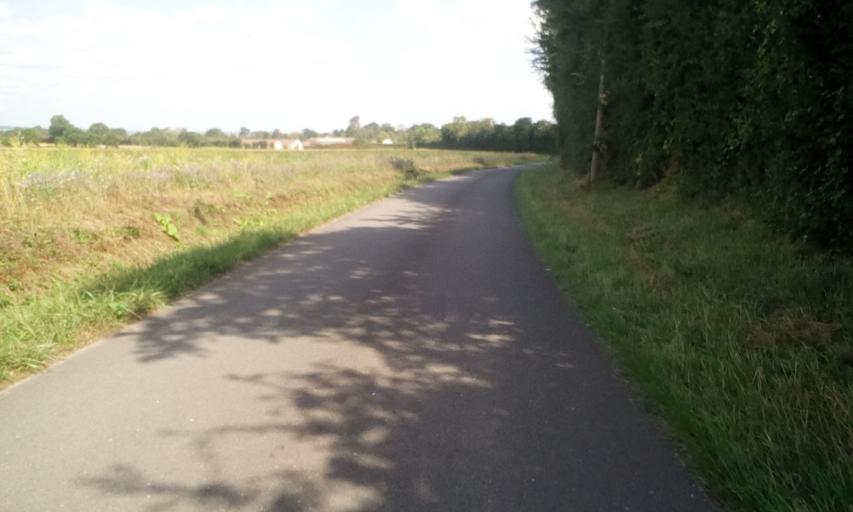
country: FR
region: Lower Normandy
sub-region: Departement du Calvados
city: Argences
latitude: 49.1323
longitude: -0.1209
